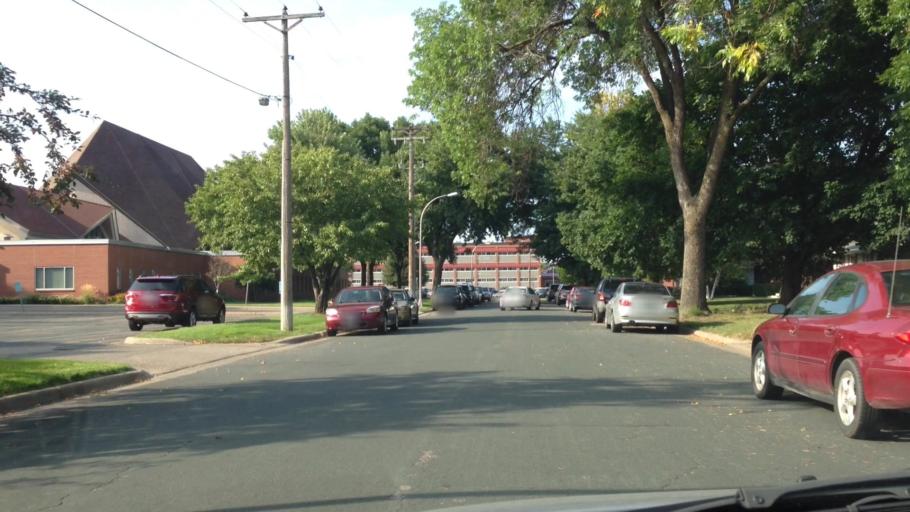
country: US
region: Minnesota
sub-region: Hennepin County
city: Bloomington
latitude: 44.8660
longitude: -93.3061
